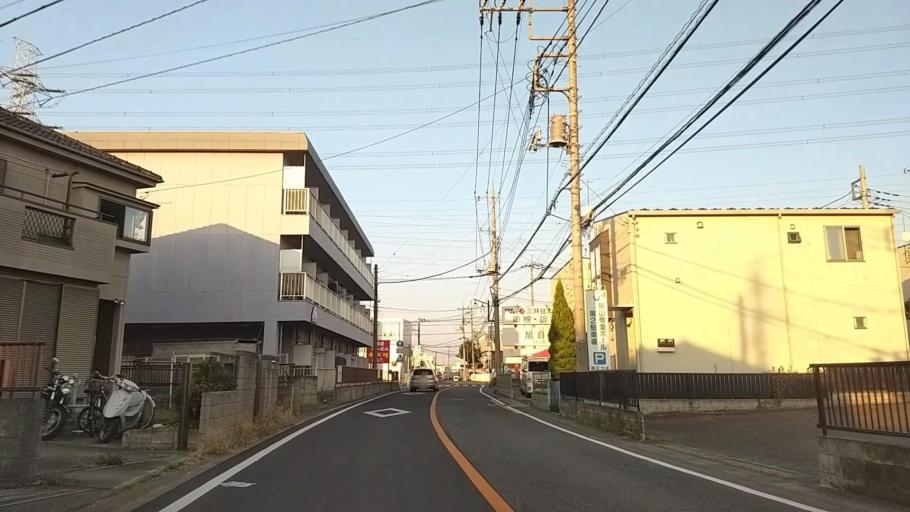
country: JP
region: Saitama
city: Sayama
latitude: 35.8700
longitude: 139.4233
